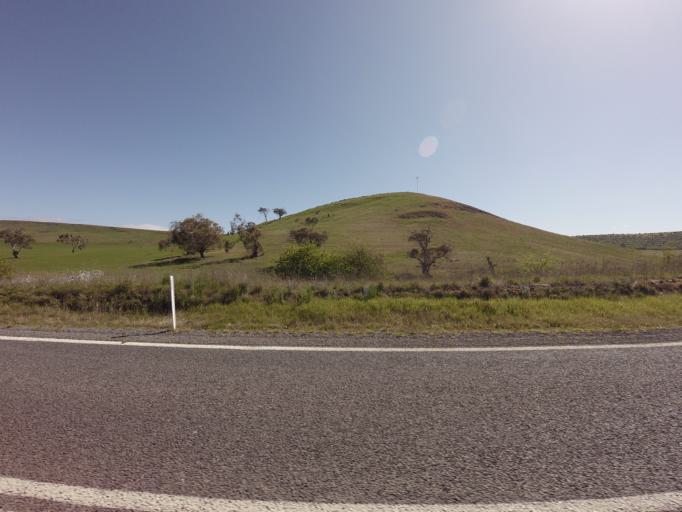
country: AU
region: Tasmania
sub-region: Derwent Valley
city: New Norfolk
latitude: -42.5739
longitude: 146.8821
